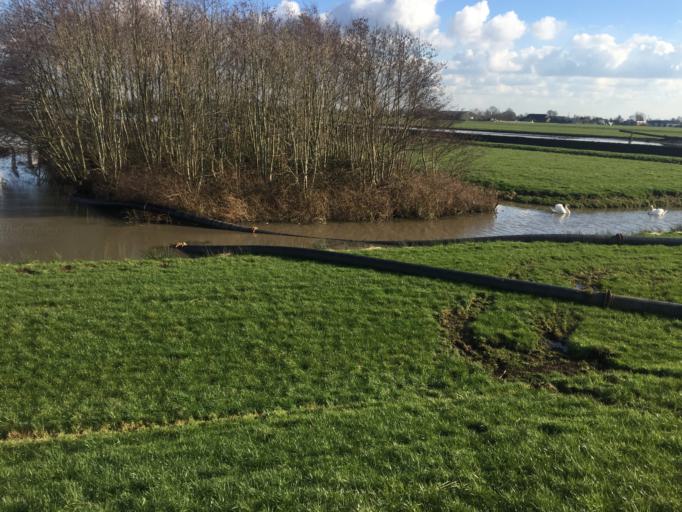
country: NL
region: South Holland
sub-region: Bodegraven-Reeuwijk
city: Bodegraven
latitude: 52.0600
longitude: 4.8041
